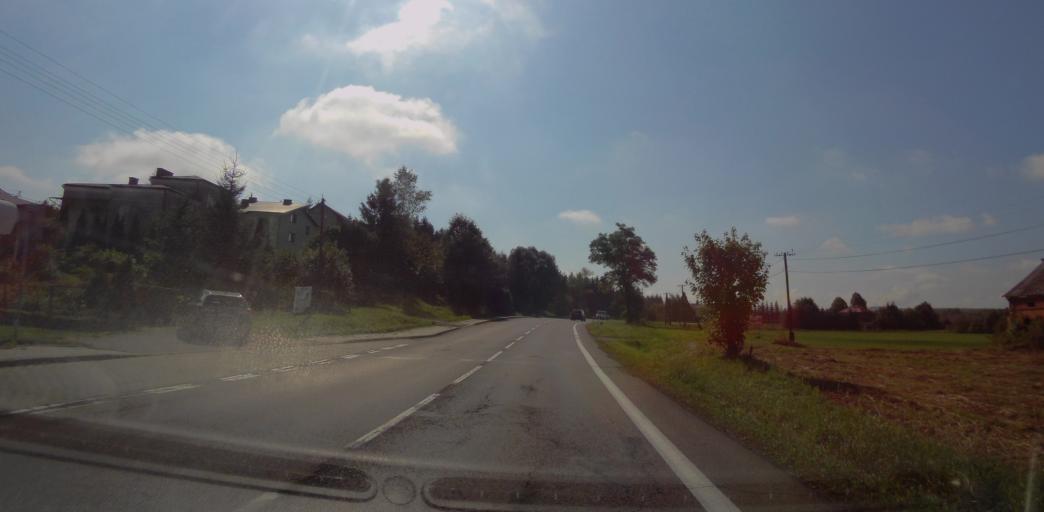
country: PL
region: Subcarpathian Voivodeship
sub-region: Powiat sanocki
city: Strachocina
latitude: 49.5972
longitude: 22.1351
